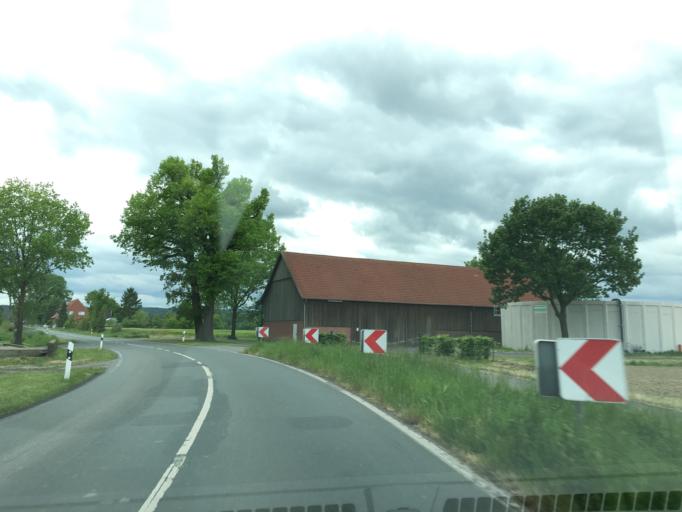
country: DE
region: North Rhine-Westphalia
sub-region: Regierungsbezirk Munster
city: Havixbeck
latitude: 51.9457
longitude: 7.4746
